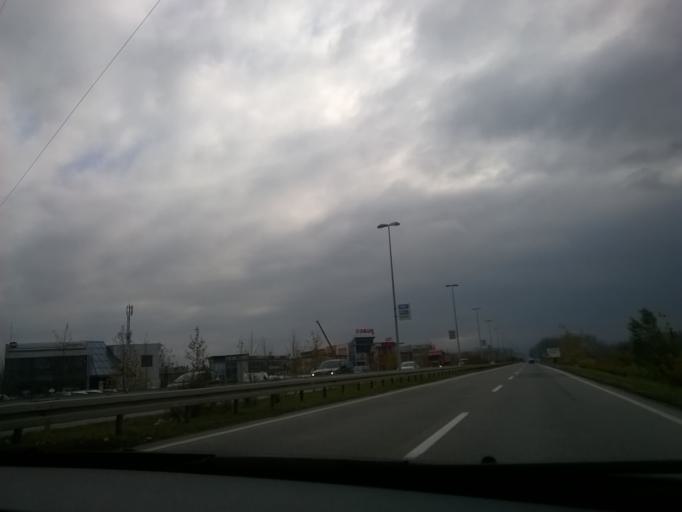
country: RS
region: Autonomna Pokrajina Vojvodina
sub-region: Juznobacki Okrug
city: Novi Sad
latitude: 45.2919
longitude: 19.8530
